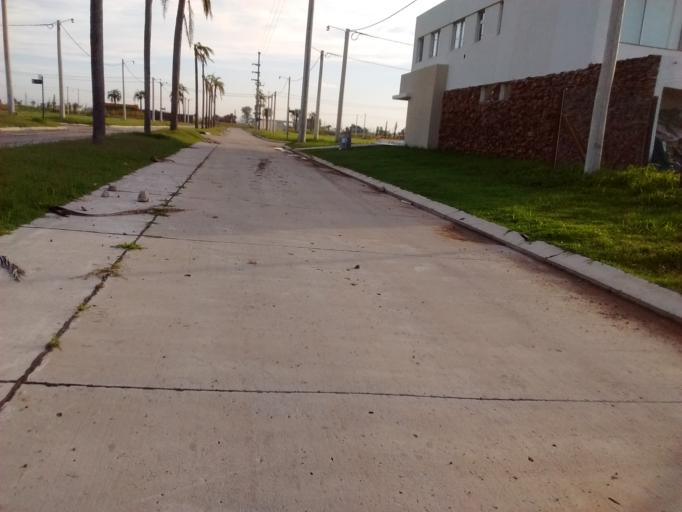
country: AR
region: Santa Fe
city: Roldan
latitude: -32.9276
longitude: -60.8744
